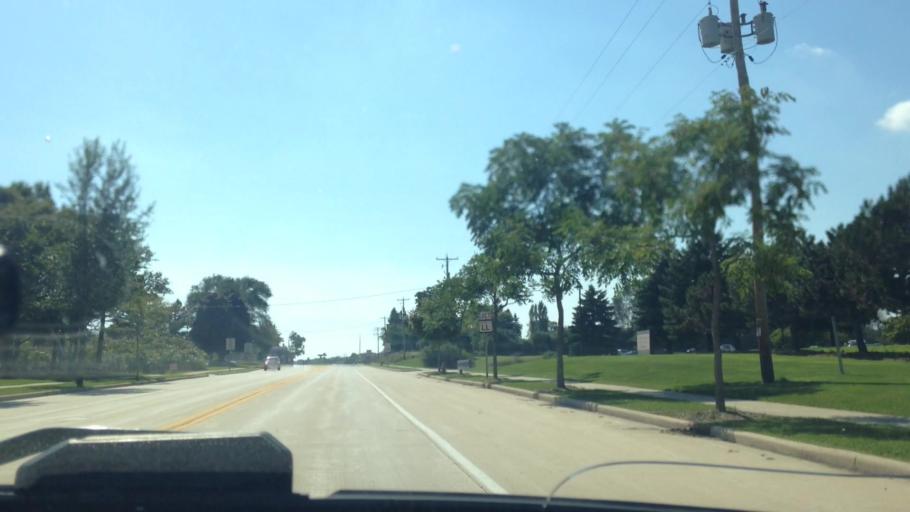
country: US
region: Wisconsin
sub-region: Ozaukee County
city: Port Washington
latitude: 43.3736
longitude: -87.8960
